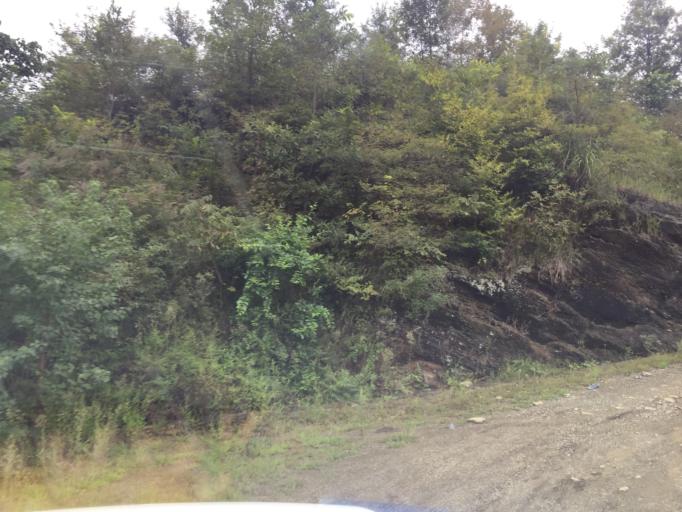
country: CN
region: Guizhou Sheng
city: Jingjiao
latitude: 28.3333
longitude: 108.1312
